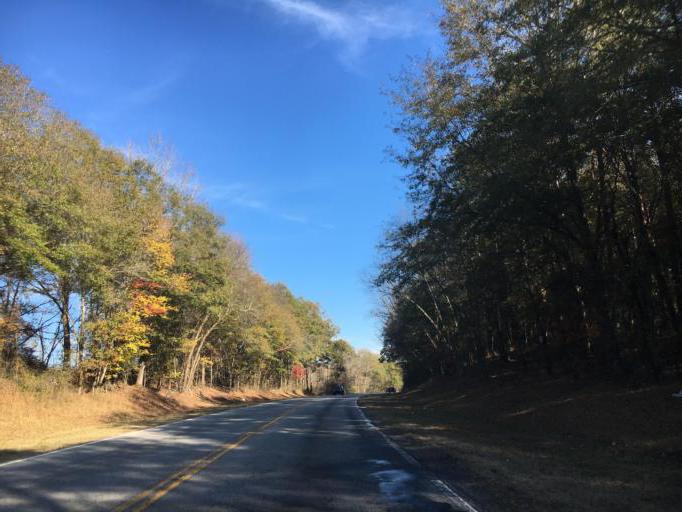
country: US
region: South Carolina
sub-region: Spartanburg County
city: Wellford
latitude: 34.9691
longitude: -82.0973
